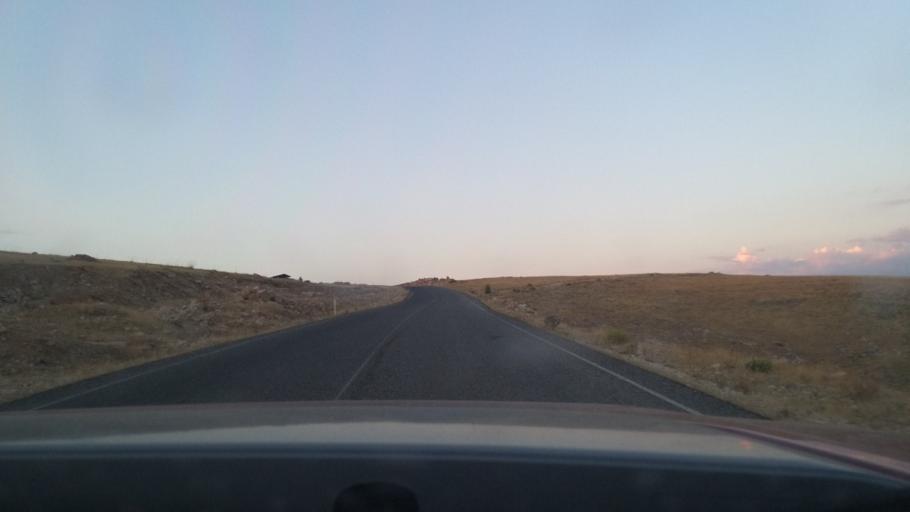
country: TR
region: Batman
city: Erkoklu
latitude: 37.7817
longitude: 41.1352
